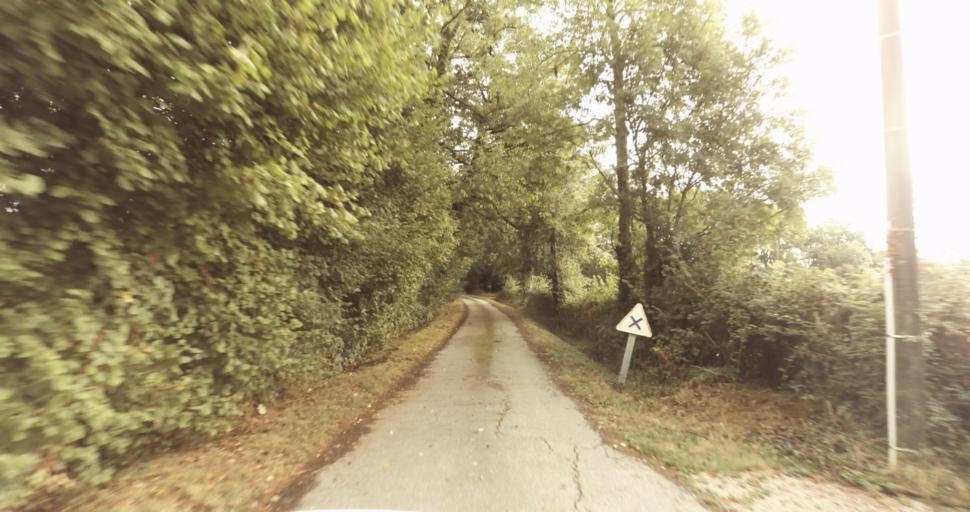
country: FR
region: Lower Normandy
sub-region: Departement du Calvados
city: Livarot
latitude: 48.9381
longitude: 0.0874
